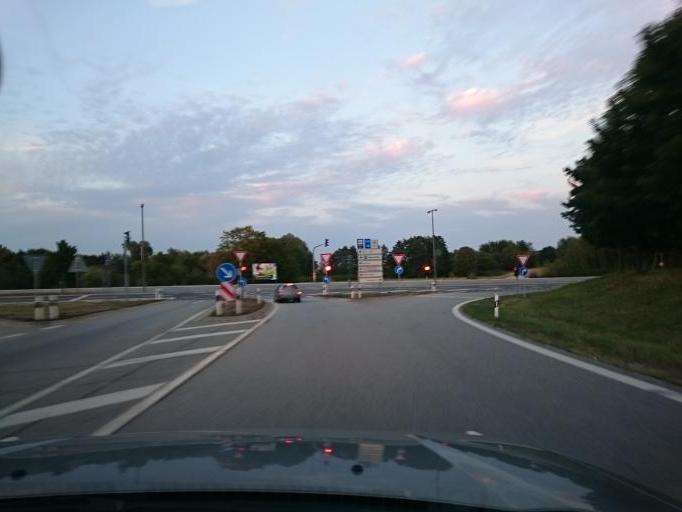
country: DE
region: Bavaria
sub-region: Upper Palatinate
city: Regensburg
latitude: 48.9965
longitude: 12.1323
